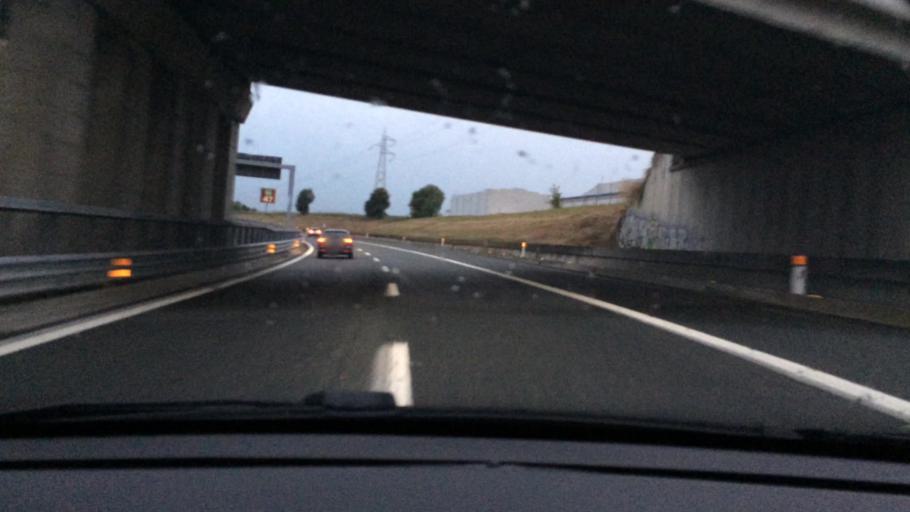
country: IT
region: Piedmont
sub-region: Provincia di Torino
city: Pasta
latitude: 45.0046
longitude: 7.5653
